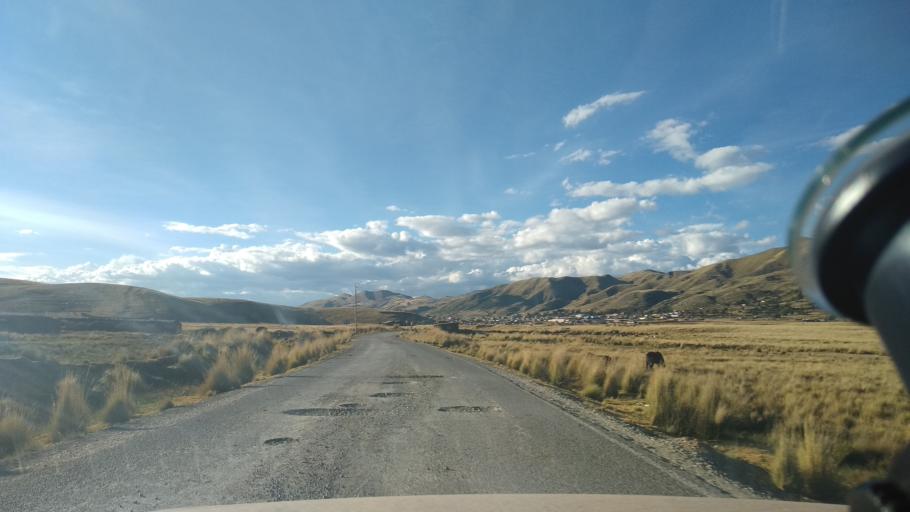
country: PE
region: Cusco
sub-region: Provincia de Canas
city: Chignayhua
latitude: -14.2369
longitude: -71.4326
